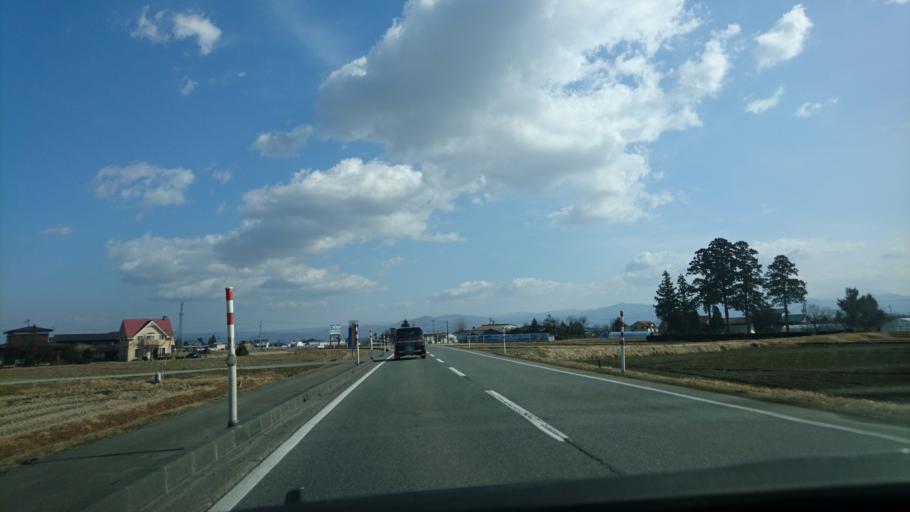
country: JP
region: Iwate
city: Morioka-shi
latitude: 39.5577
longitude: 141.1049
